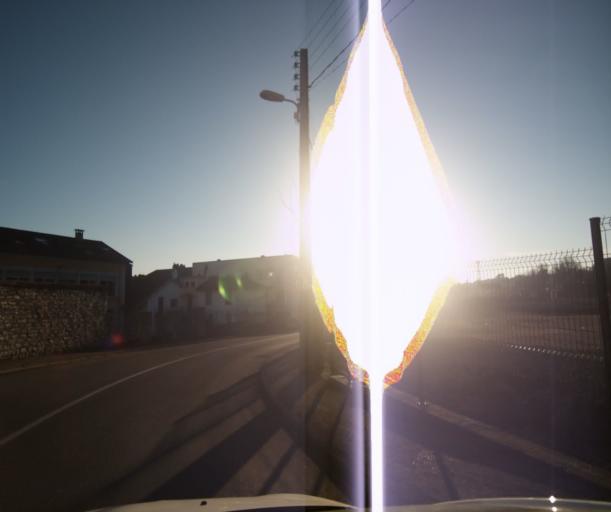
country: FR
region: Franche-Comte
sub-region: Departement du Doubs
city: Besancon
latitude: 47.2509
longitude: 6.0303
